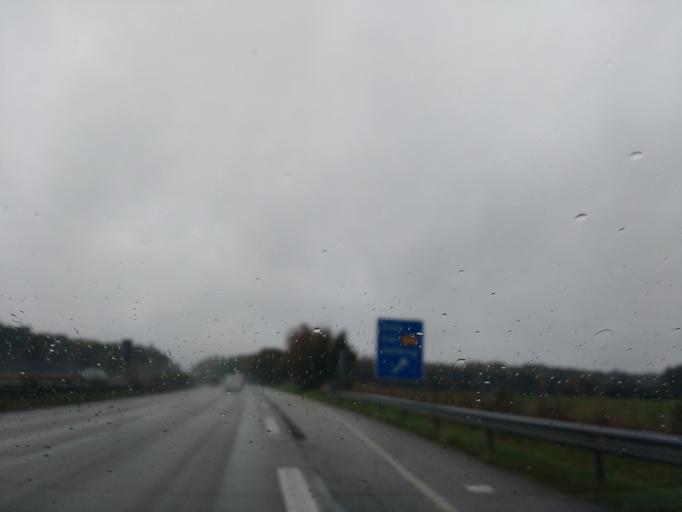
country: DE
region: Schleswig-Holstein
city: Susel
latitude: 54.0567
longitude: 10.7390
